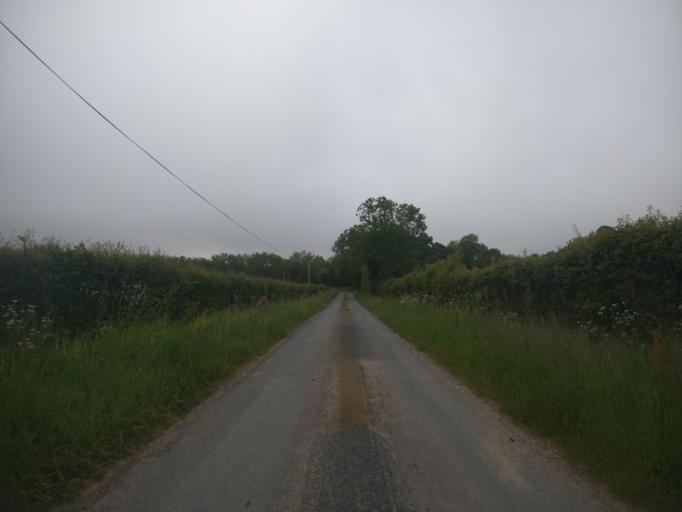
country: FR
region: Poitou-Charentes
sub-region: Departement des Deux-Sevres
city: Chiche
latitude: 46.8948
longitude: -0.3441
